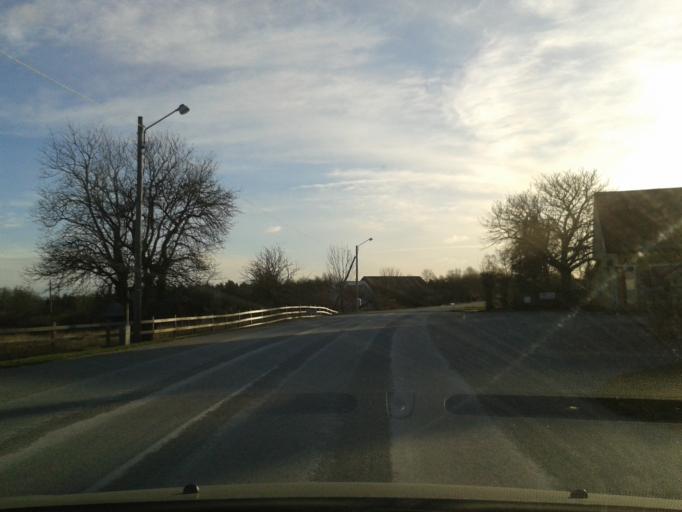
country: SE
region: Gotland
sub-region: Gotland
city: Hemse
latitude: 57.4285
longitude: 18.6312
